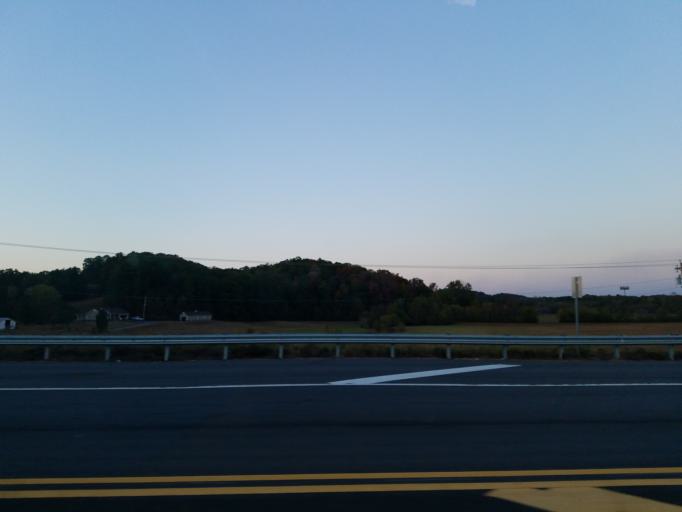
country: US
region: Georgia
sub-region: Gordon County
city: Calhoun
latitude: 34.5759
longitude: -84.9560
